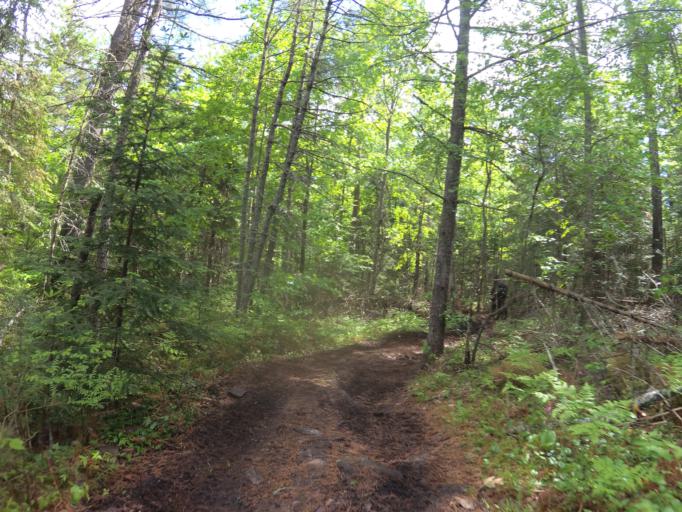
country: CA
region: Ontario
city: Renfrew
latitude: 45.1239
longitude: -76.8439
